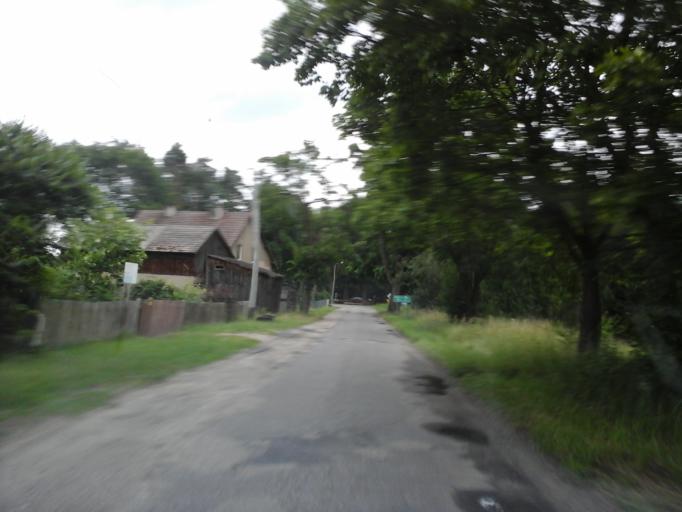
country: PL
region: West Pomeranian Voivodeship
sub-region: Powiat choszczenski
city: Bierzwnik
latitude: 53.0112
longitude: 15.6382
